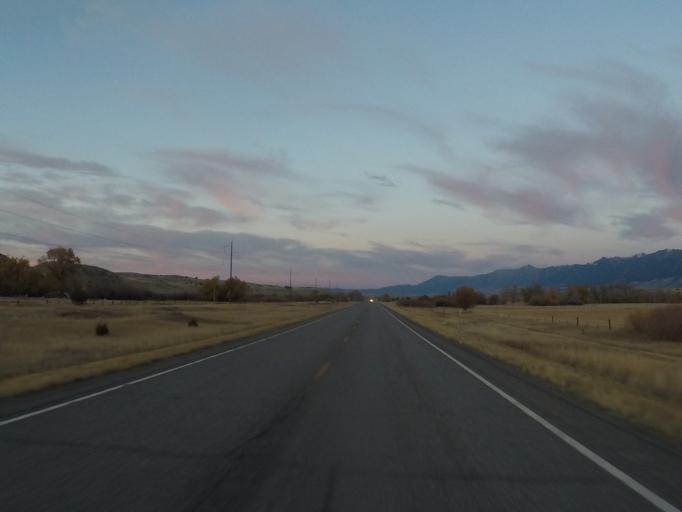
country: US
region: Montana
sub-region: Park County
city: Livingston
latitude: 45.3569
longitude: -110.7450
